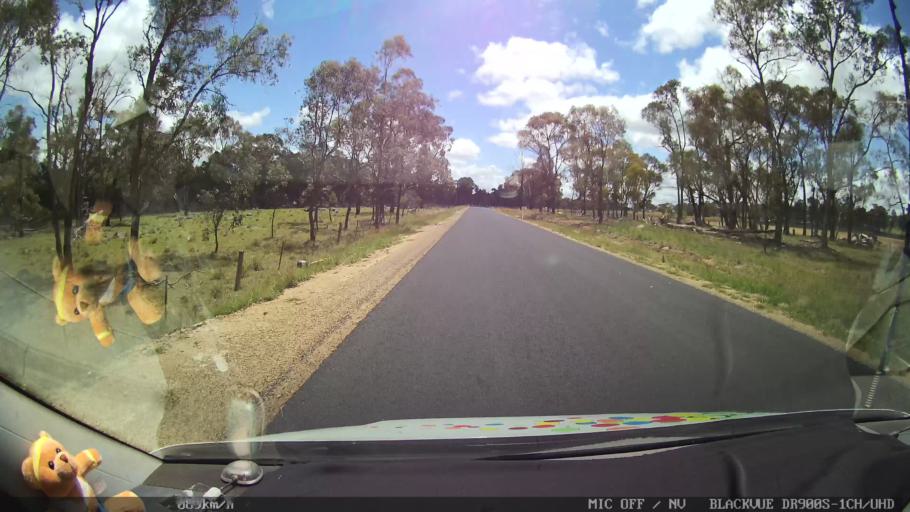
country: AU
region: New South Wales
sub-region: Glen Innes Severn
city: Glen Innes
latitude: -29.4267
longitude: 151.7030
